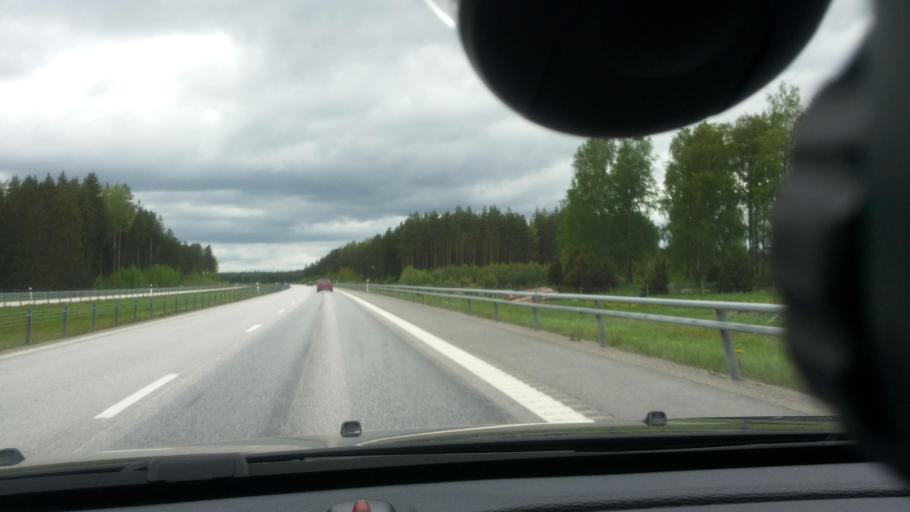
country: SE
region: Uppsala
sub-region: Osthammars Kommun
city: Bjorklinge
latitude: 60.0732
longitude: 17.6066
